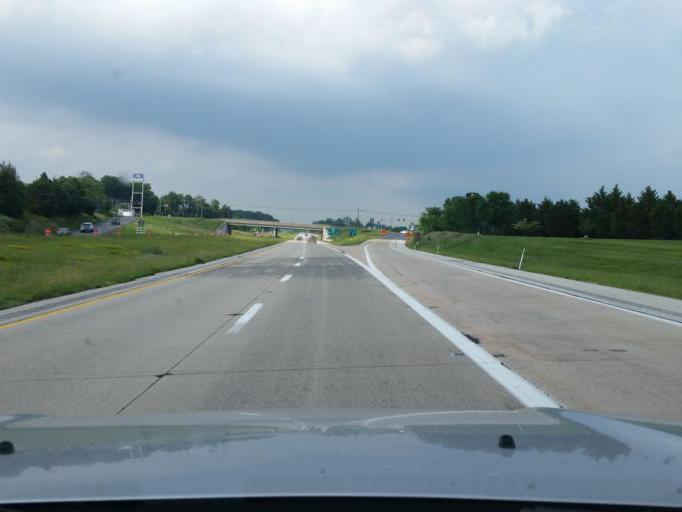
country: US
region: Pennsylvania
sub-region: Adams County
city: Lake Heritage
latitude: 39.7966
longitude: -77.2026
